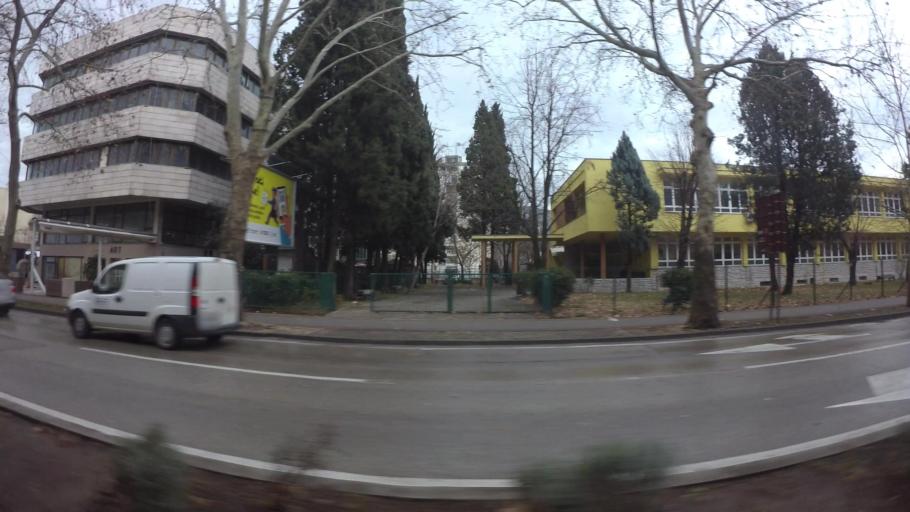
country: BA
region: Federation of Bosnia and Herzegovina
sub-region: Hercegovacko-Bosanski Kanton
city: Mostar
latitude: 43.3458
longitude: 17.7995
